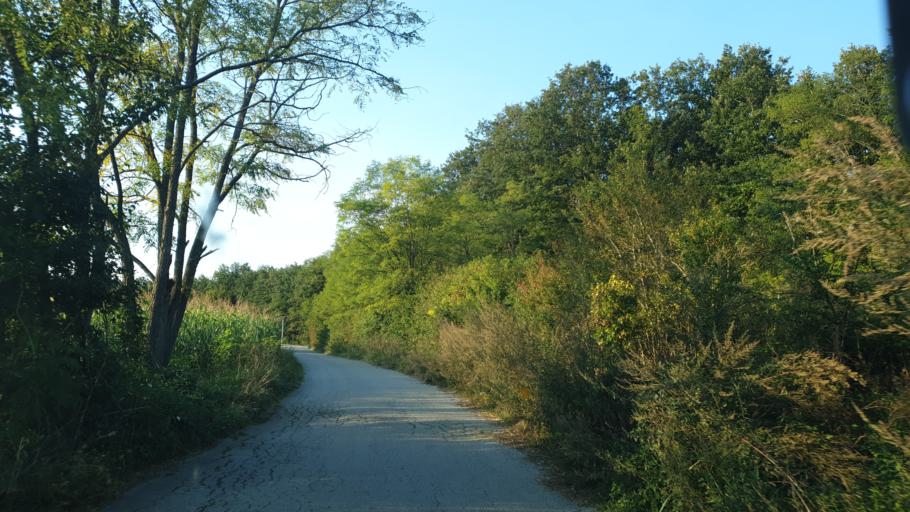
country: RS
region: Central Serbia
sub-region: Zlatiborski Okrug
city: Kosjeric
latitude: 43.9790
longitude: 20.0153
